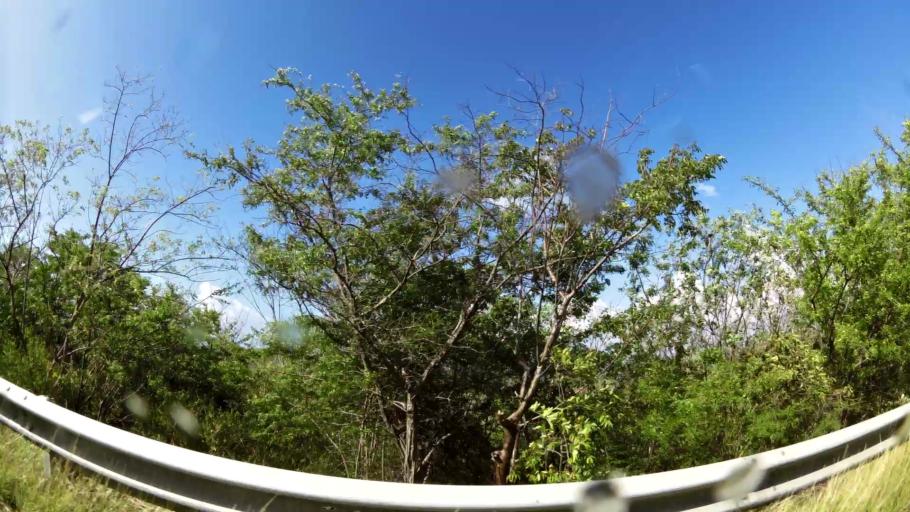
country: MQ
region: Martinique
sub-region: Martinique
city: Les Trois-Ilets
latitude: 14.4596
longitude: -61.0655
